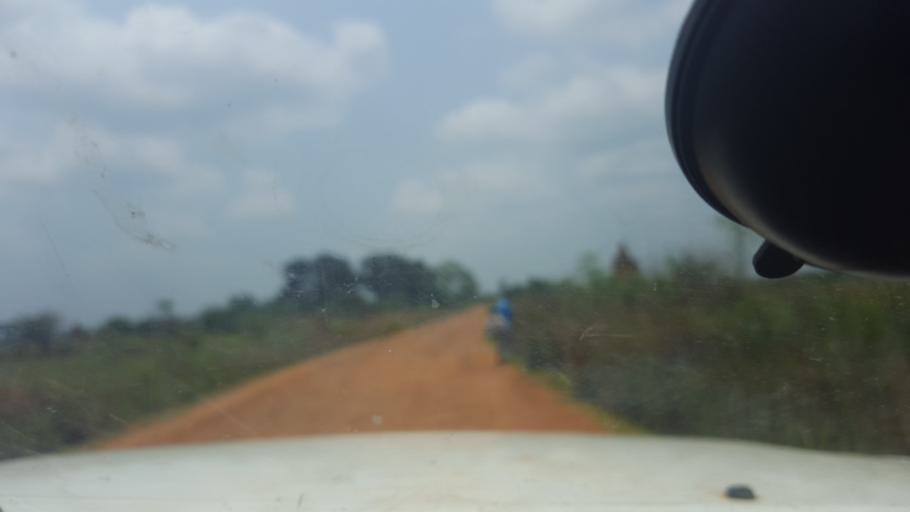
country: CD
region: Bandundu
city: Bandundu
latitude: -3.3328
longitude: 17.2846
